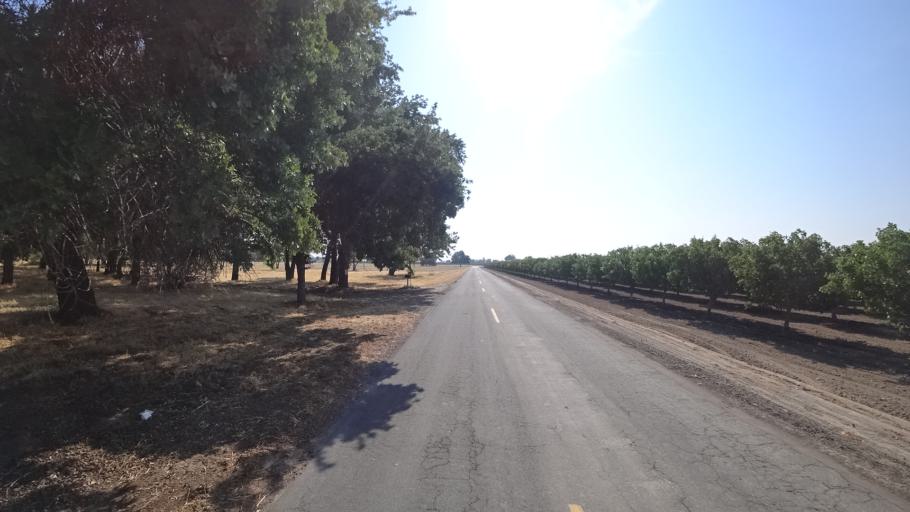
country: US
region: California
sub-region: Kings County
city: Lemoore
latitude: 36.3285
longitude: -119.8557
